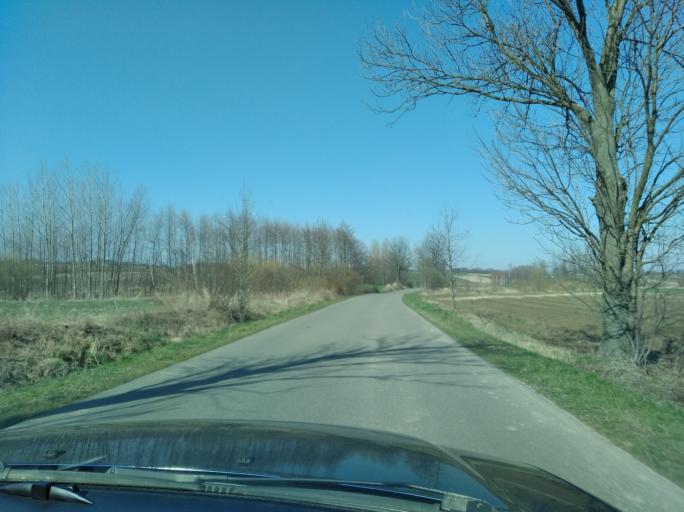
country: PL
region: Subcarpathian Voivodeship
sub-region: Powiat przeworski
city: Pantalowice
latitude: 49.9406
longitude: 22.4422
